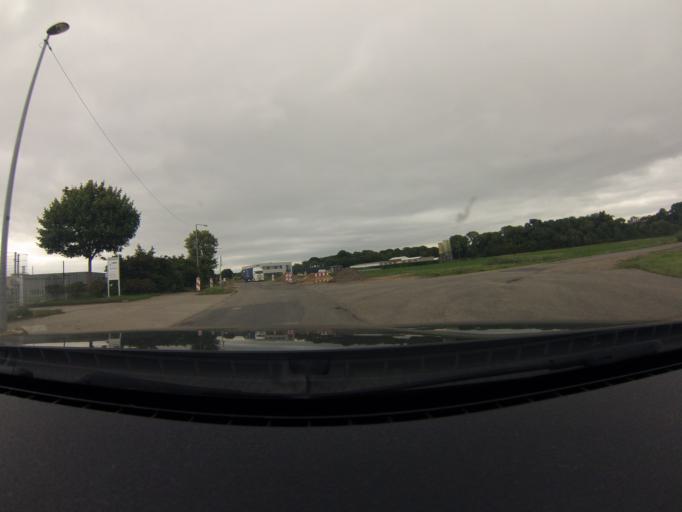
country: DE
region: North Rhine-Westphalia
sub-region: Regierungsbezirk Koln
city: Hurth
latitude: 50.9111
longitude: 6.8573
